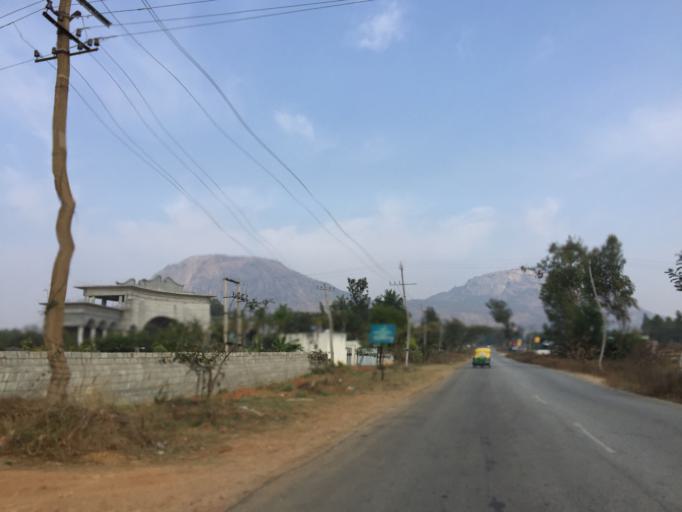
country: IN
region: Karnataka
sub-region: Bangalore Rural
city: Devanhalli
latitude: 13.3349
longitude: 77.6899
